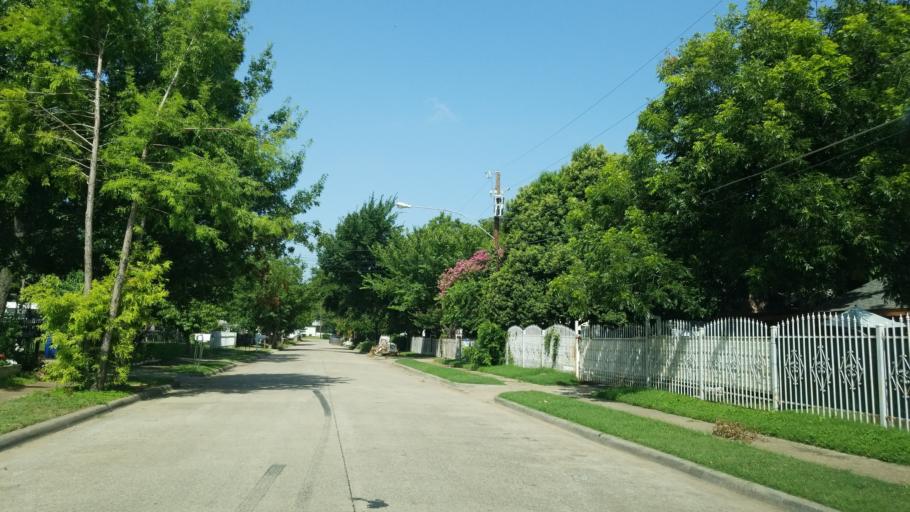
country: US
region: Texas
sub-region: Dallas County
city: Cockrell Hill
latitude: 32.7779
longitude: -96.9100
